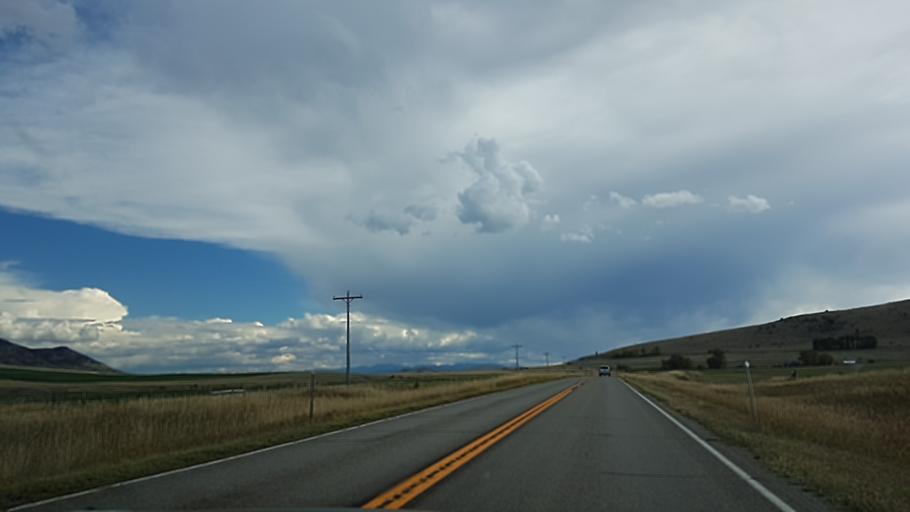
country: US
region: Montana
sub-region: Jefferson County
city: Whitehall
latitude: 45.7854
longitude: -111.9165
